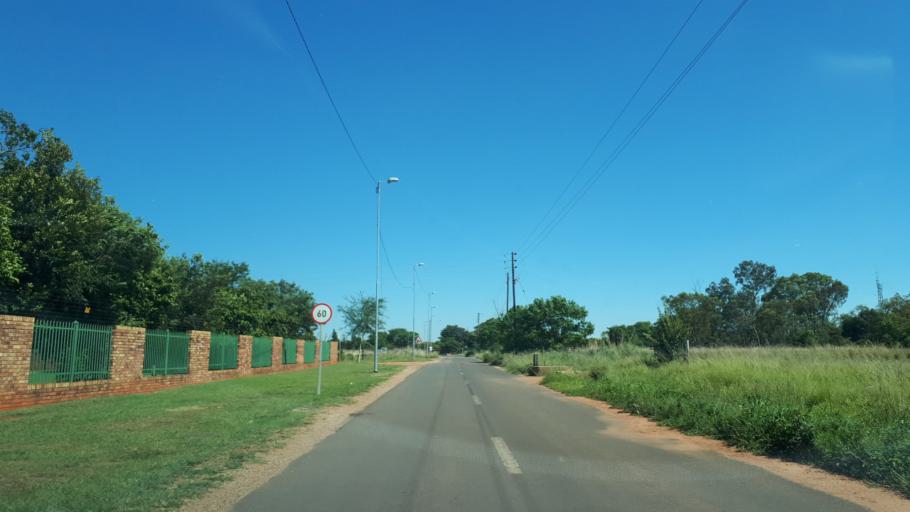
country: ZA
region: Gauteng
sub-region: City of Tshwane Metropolitan Municipality
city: Centurion
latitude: -25.8115
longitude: 28.3547
